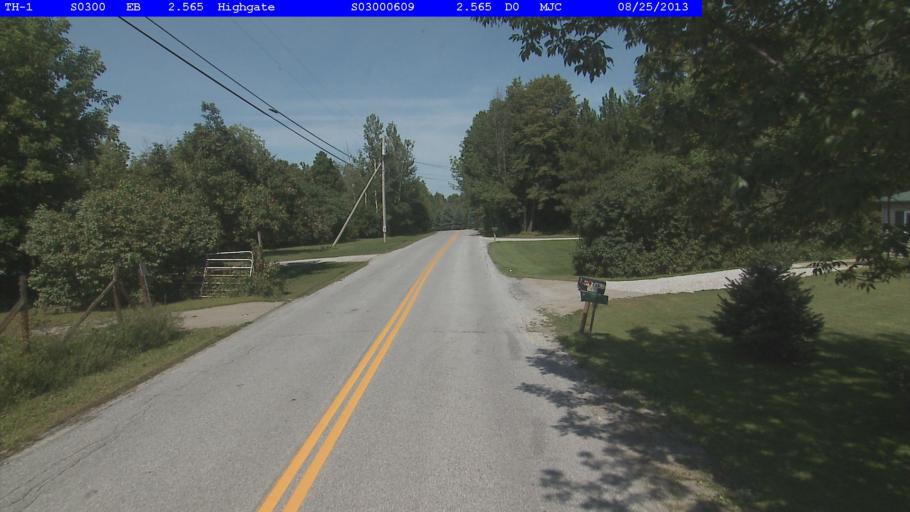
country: US
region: Vermont
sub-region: Franklin County
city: Swanton
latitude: 44.9605
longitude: -73.0941
